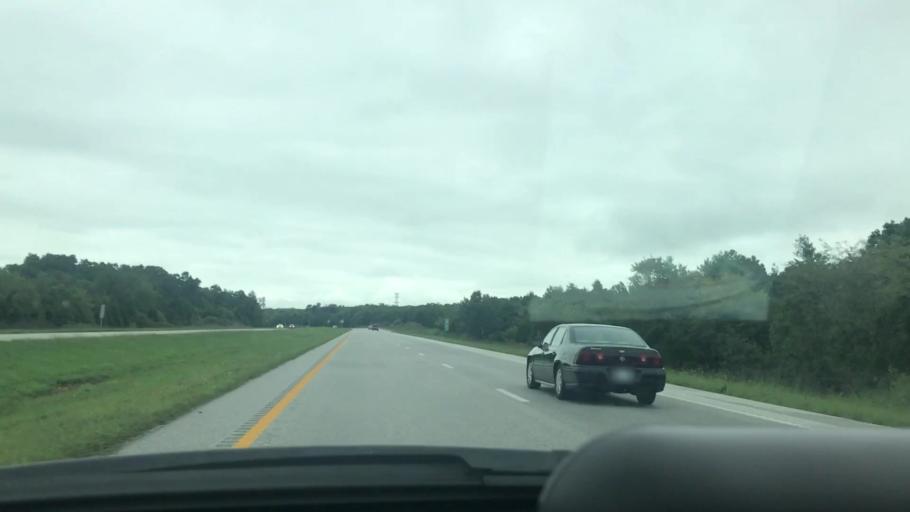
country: US
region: Missouri
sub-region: Greene County
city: Fair Grove
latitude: 37.3163
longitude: -93.1699
